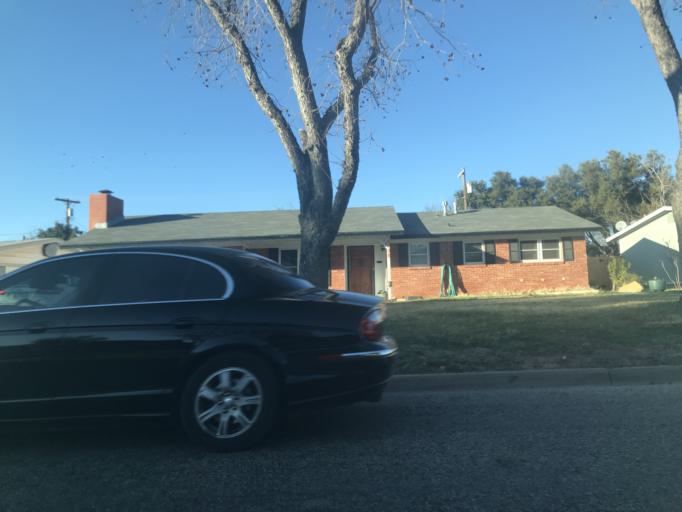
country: US
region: Texas
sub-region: Tom Green County
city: San Angelo
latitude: 31.4384
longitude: -100.4770
